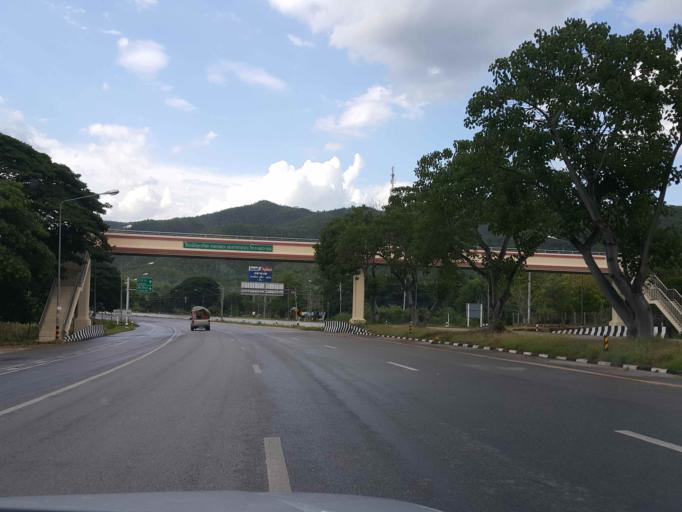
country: TH
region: Lampang
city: Thoen
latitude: 17.6535
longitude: 99.2506
